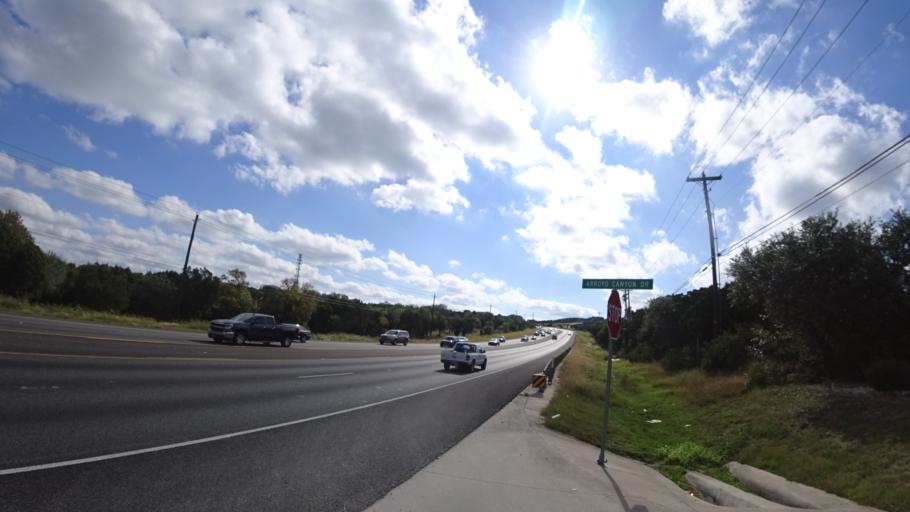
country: US
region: Texas
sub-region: Travis County
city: Bee Cave
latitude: 30.2847
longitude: -97.9169
